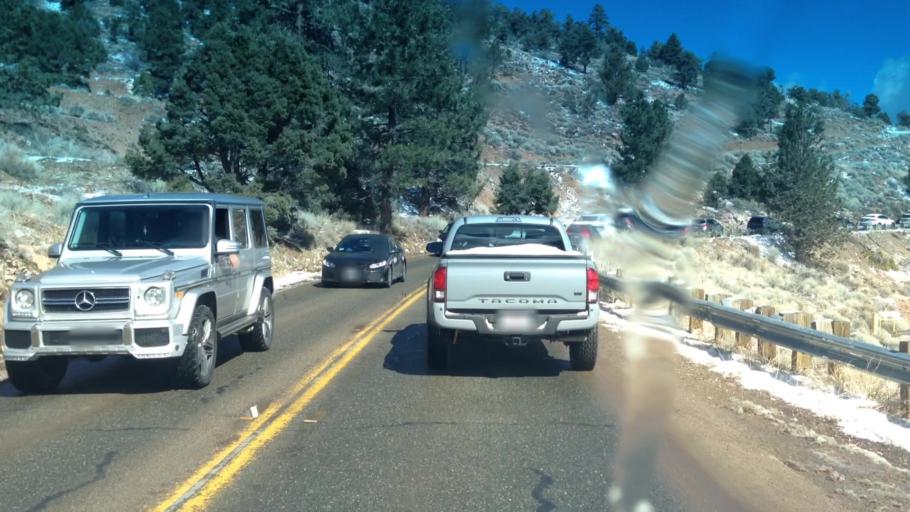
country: US
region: California
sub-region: San Bernardino County
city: Big Bear City
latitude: 34.2747
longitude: -116.8190
